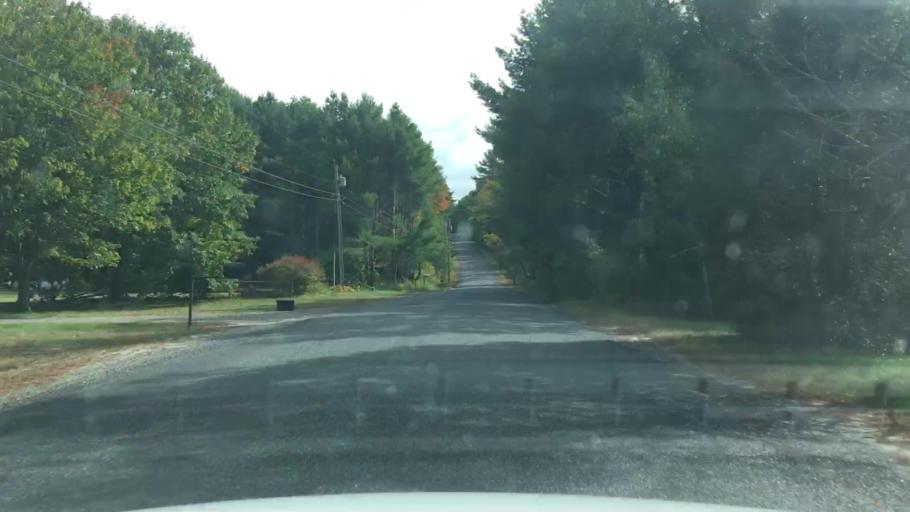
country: US
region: Maine
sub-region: Androscoggin County
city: Lisbon Falls
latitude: 43.9779
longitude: -70.0923
